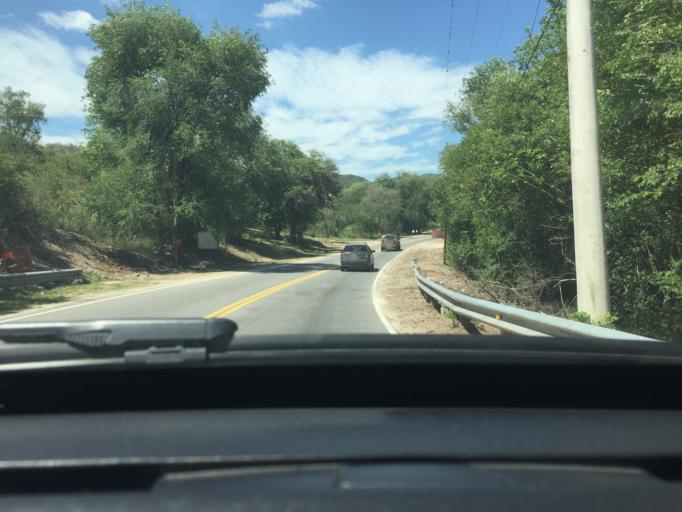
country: AR
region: Cordoba
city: Alta Gracia
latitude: -31.7350
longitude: -64.4498
